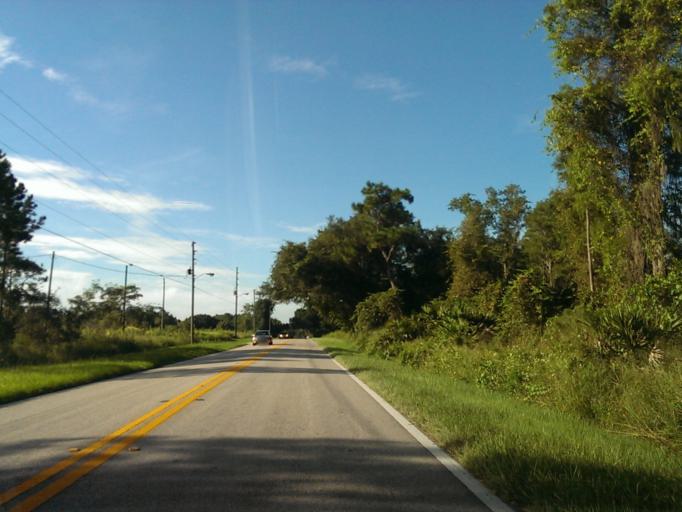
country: US
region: Florida
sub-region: Polk County
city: Citrus Ridge
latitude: 28.3696
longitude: -81.6457
